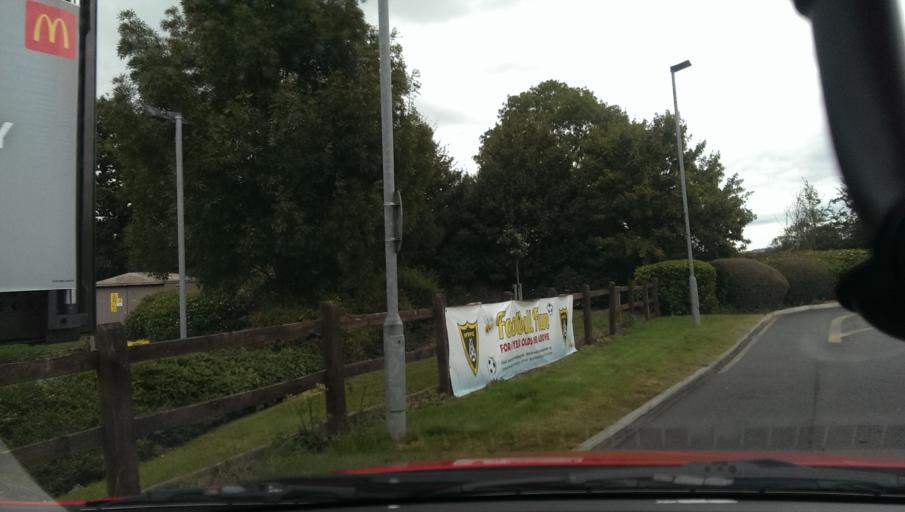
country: GB
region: England
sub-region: Leicestershire
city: Market Harborough
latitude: 52.5114
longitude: -0.9415
